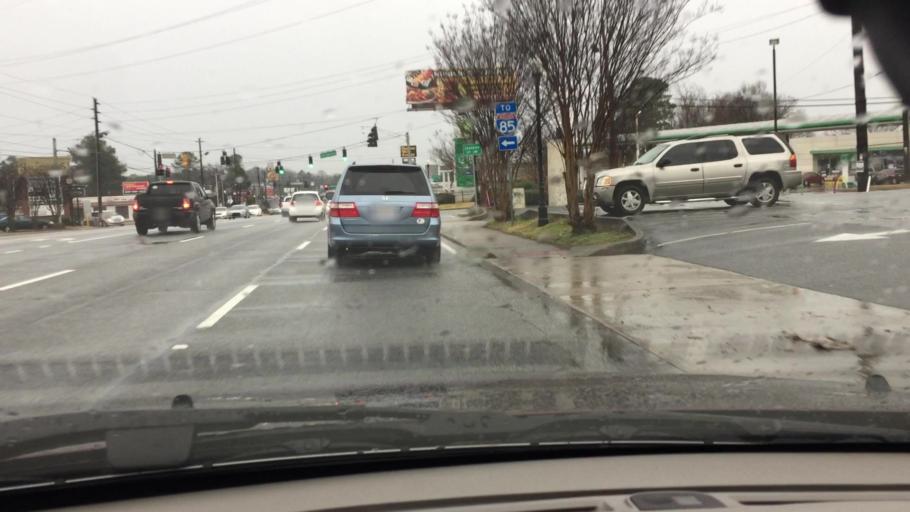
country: US
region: Georgia
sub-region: DeKalb County
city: Doraville
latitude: 33.8907
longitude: -84.2856
